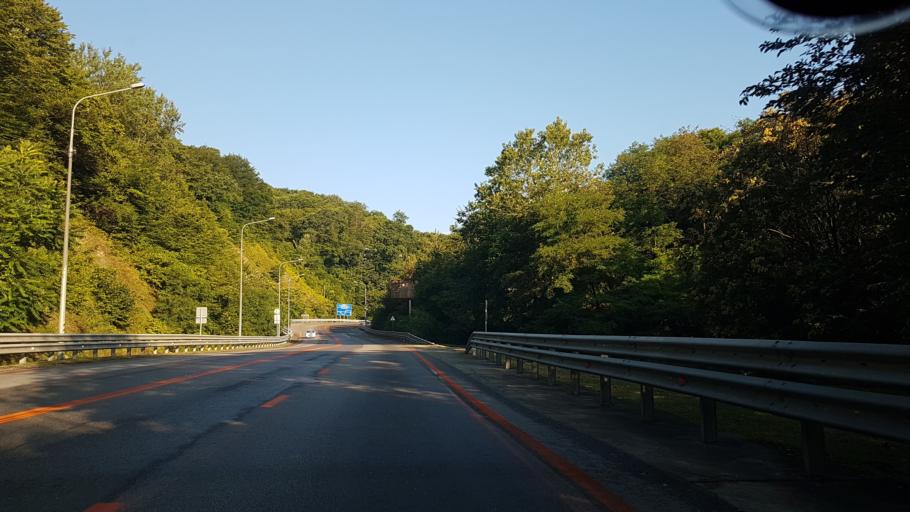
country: RU
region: Krasnodarskiy
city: Dagomys
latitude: 43.6462
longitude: 39.6930
